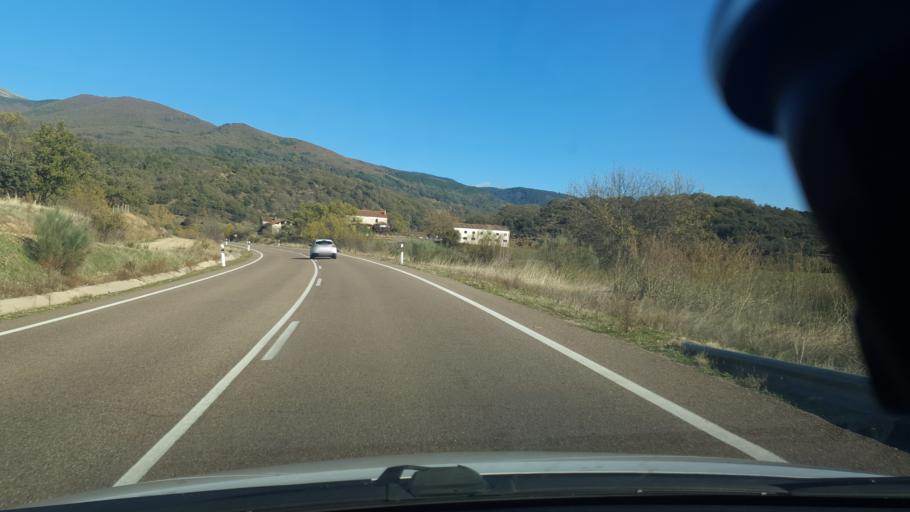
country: ES
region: Castille and Leon
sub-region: Provincia de Avila
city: Poyales del Hoyo
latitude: 40.1486
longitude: -5.1903
